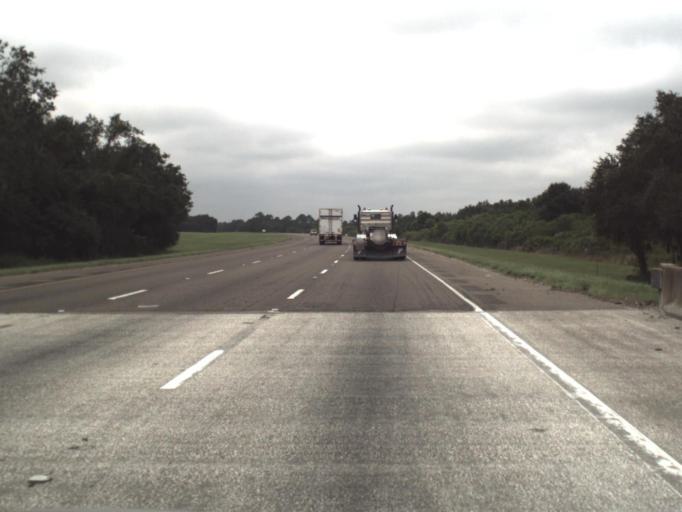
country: US
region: Florida
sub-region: Hillsborough County
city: Ruskin
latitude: 27.6419
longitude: -82.4611
